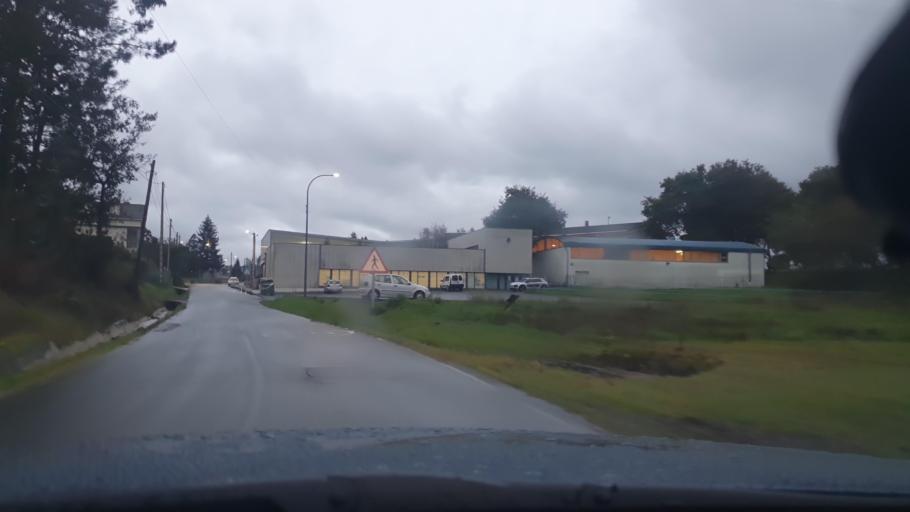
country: ES
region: Galicia
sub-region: Provincia da Coruna
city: Santiago de Compostela
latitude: 42.8522
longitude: -8.5891
